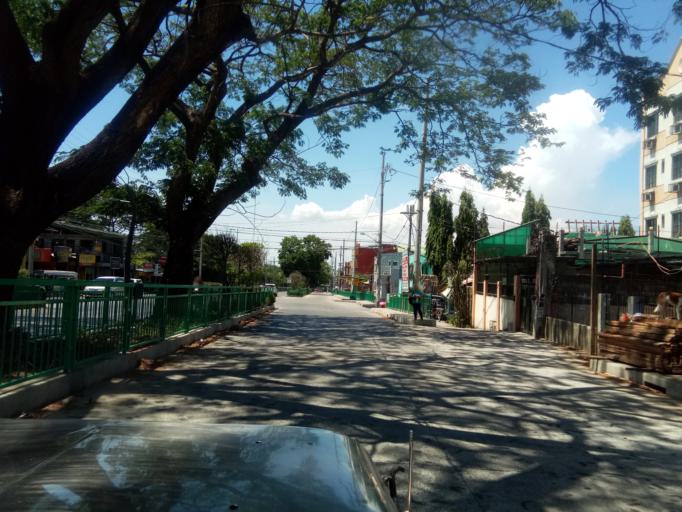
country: PH
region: Calabarzon
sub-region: Province of Cavite
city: Dasmarinas
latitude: 14.3192
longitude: 120.9641
